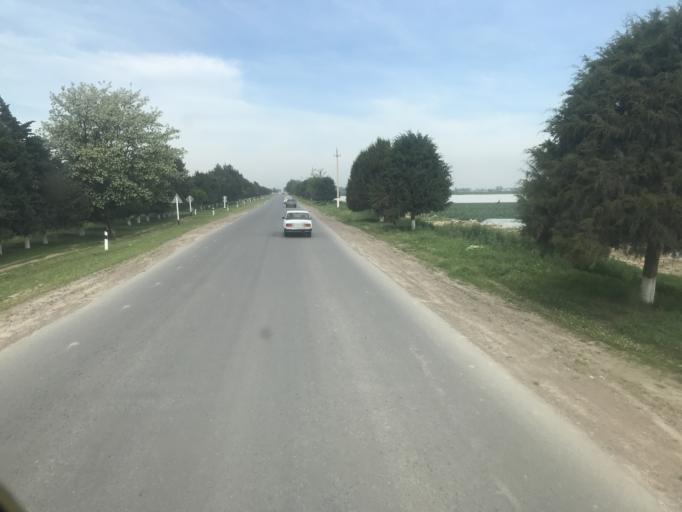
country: KZ
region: Ongtustik Qazaqstan
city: Asykata
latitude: 40.9847
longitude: 68.2945
